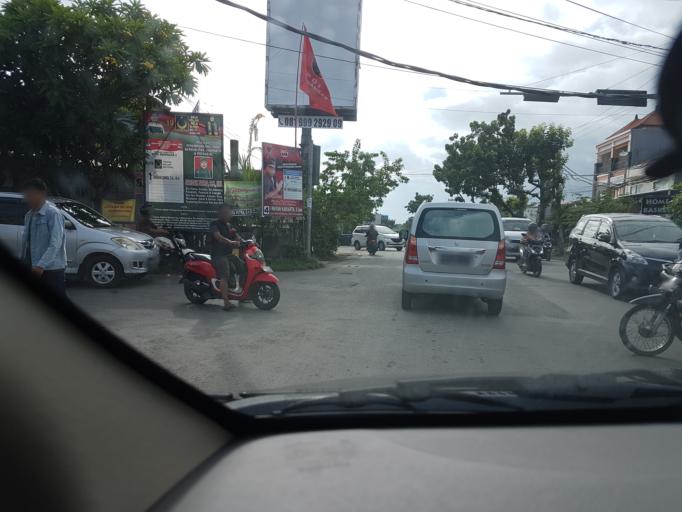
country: ID
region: Bali
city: Denpasar
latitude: -8.6733
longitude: 115.1824
